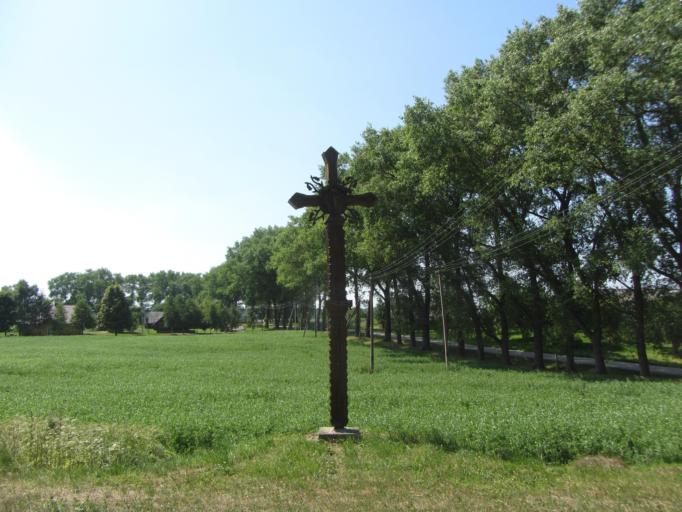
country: LT
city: Sirvintos
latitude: 55.1509
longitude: 24.9670
